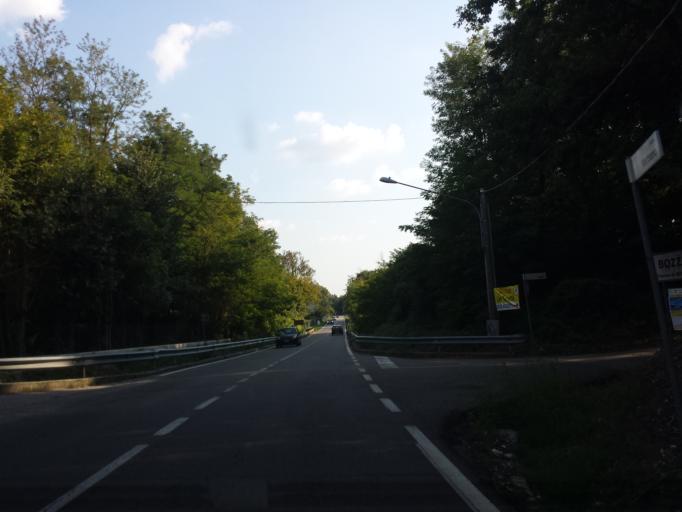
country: IT
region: Lombardy
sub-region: Provincia di Varese
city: Monvalle
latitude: 45.8421
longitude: 8.6290
